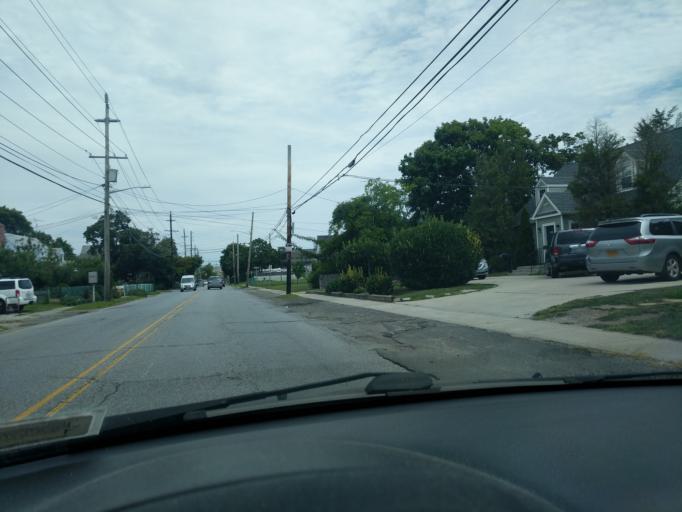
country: US
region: New York
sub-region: Nassau County
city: Woodmere
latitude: 40.6368
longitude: -73.7080
